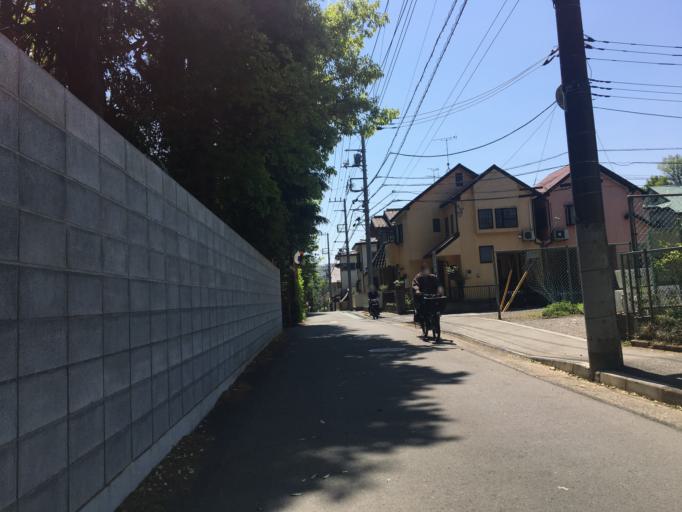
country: JP
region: Tokyo
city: Kokubunji
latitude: 35.7194
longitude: 139.5023
